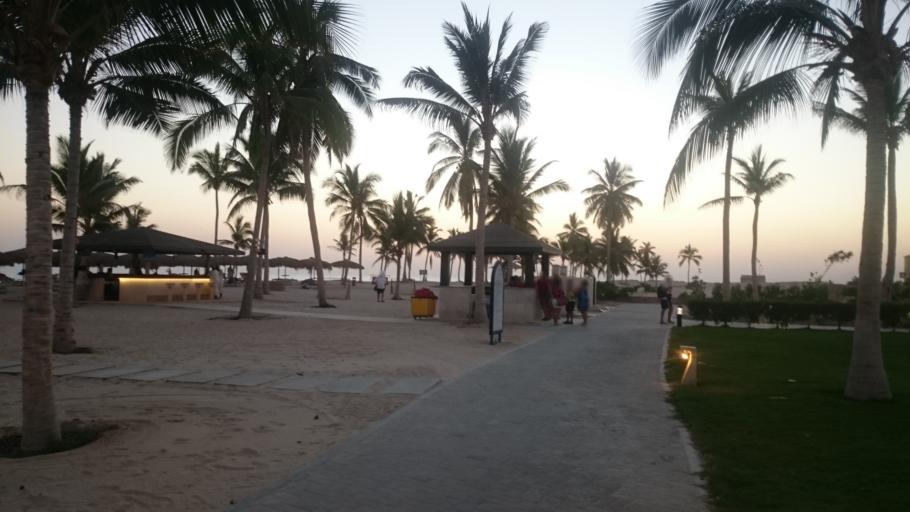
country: OM
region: Zufar
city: Salalah
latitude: 17.0290
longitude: 54.2956
